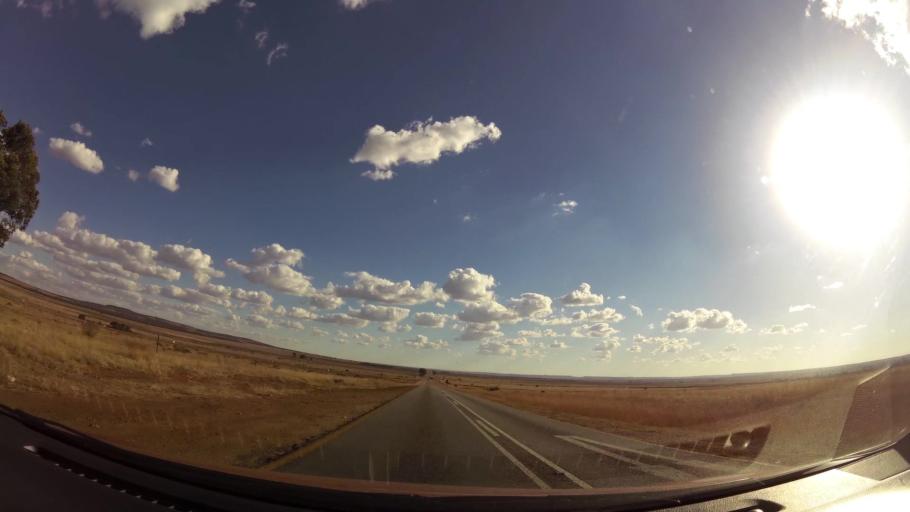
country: ZA
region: Gauteng
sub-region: West Rand District Municipality
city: Carletonville
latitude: -26.4001
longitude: 27.2922
